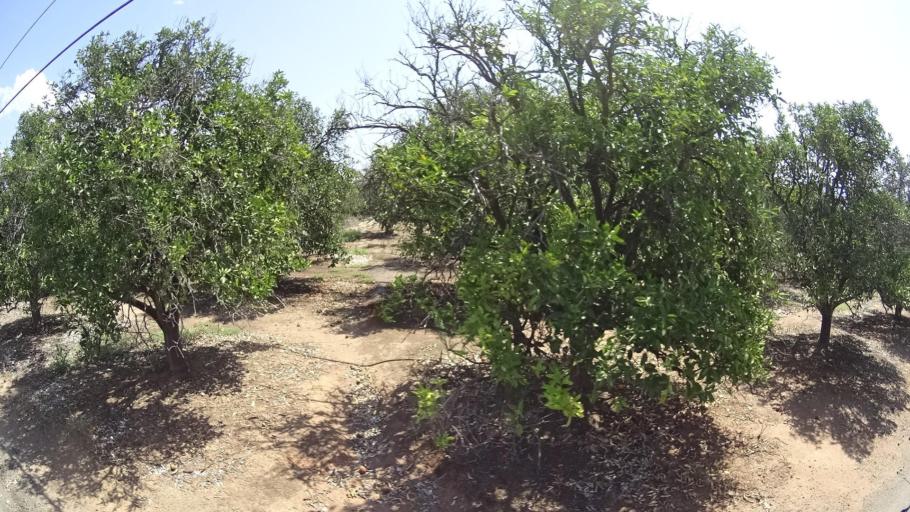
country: US
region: California
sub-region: San Diego County
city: Valley Center
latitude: 33.2405
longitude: -116.9940
